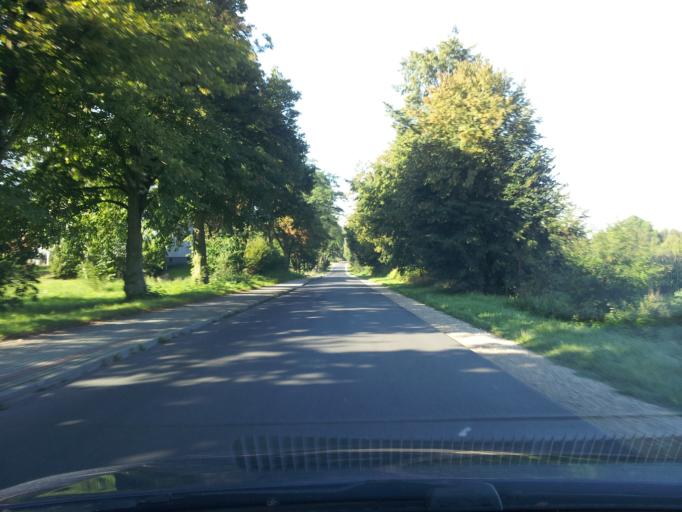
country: PL
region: Kujawsko-Pomorskie
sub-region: Powiat brodnicki
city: Swiedziebnia
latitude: 53.0875
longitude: 19.5121
